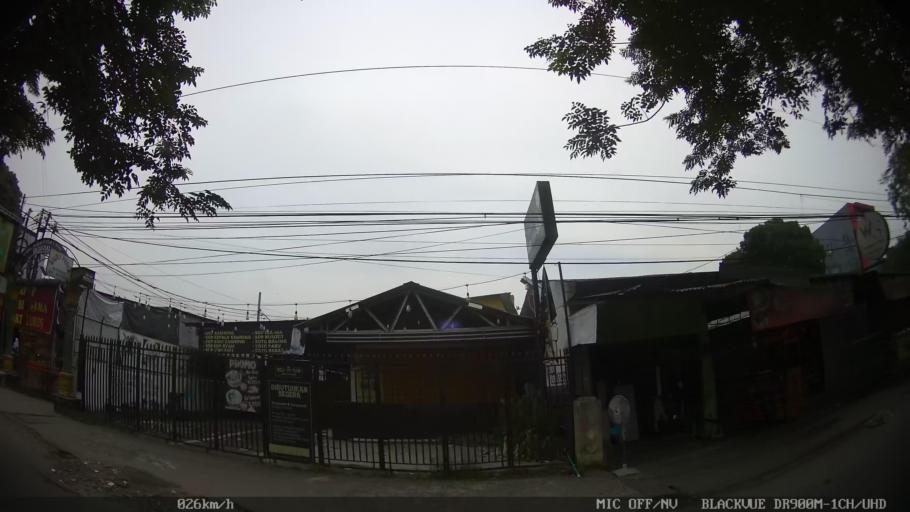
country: ID
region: North Sumatra
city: Medan
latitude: 3.5531
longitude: 98.6935
